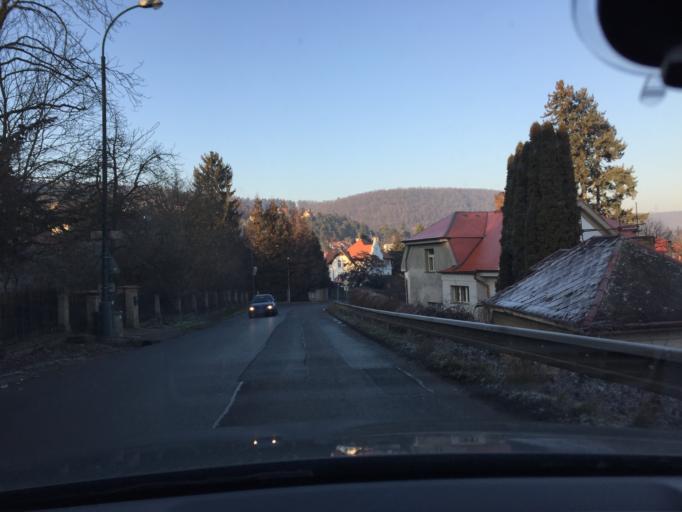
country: CZ
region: Central Bohemia
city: Cernosice
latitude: 49.9569
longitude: 14.3219
